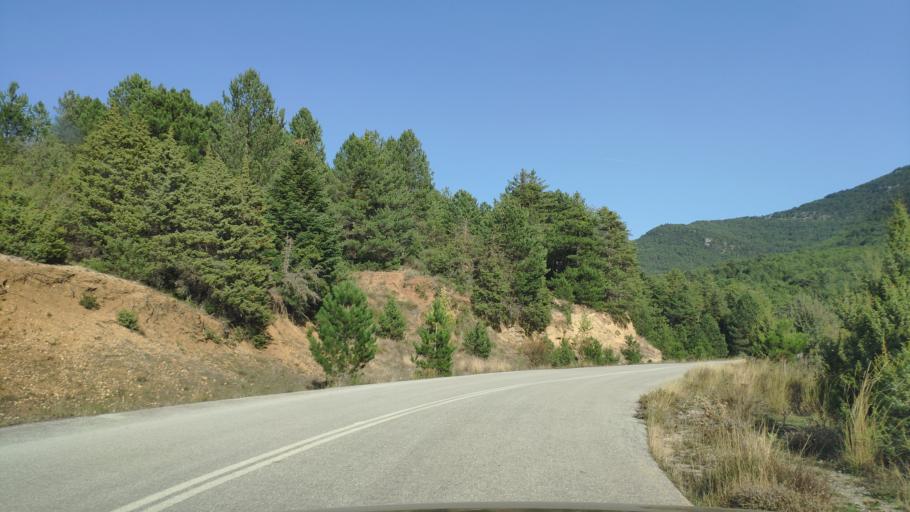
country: GR
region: West Greece
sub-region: Nomos Achaias
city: Aiyira
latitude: 37.9937
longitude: 22.3701
